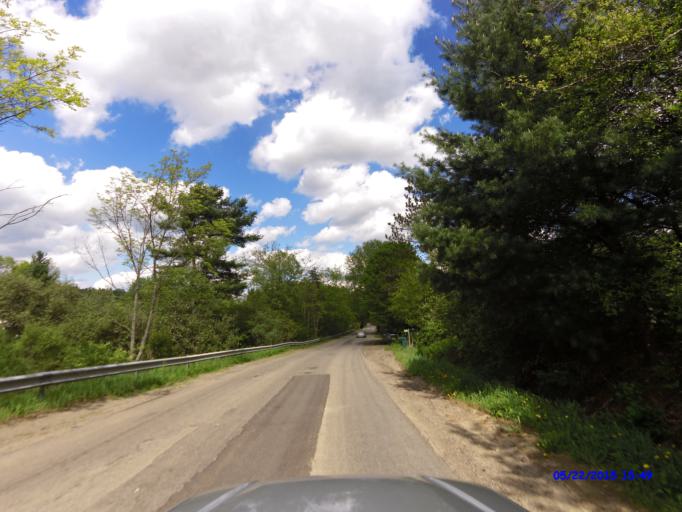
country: US
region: New York
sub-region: Cattaraugus County
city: Franklinville
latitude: 42.3363
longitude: -78.4893
